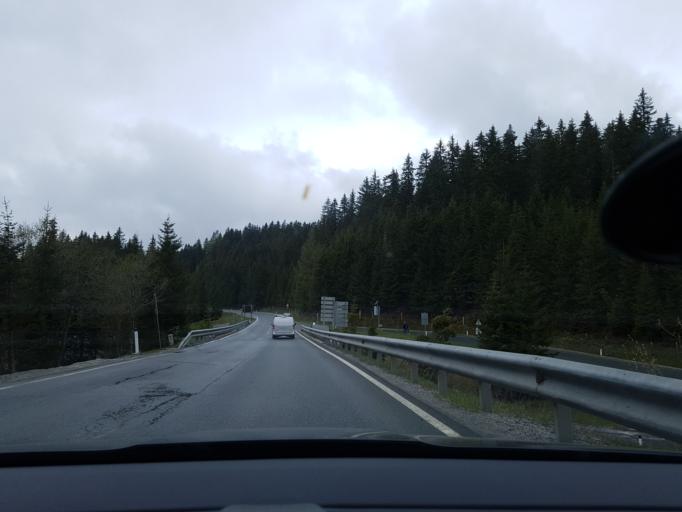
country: AT
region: Salzburg
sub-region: Politischer Bezirk Zell am See
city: Krimml
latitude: 47.2432
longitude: 12.1217
